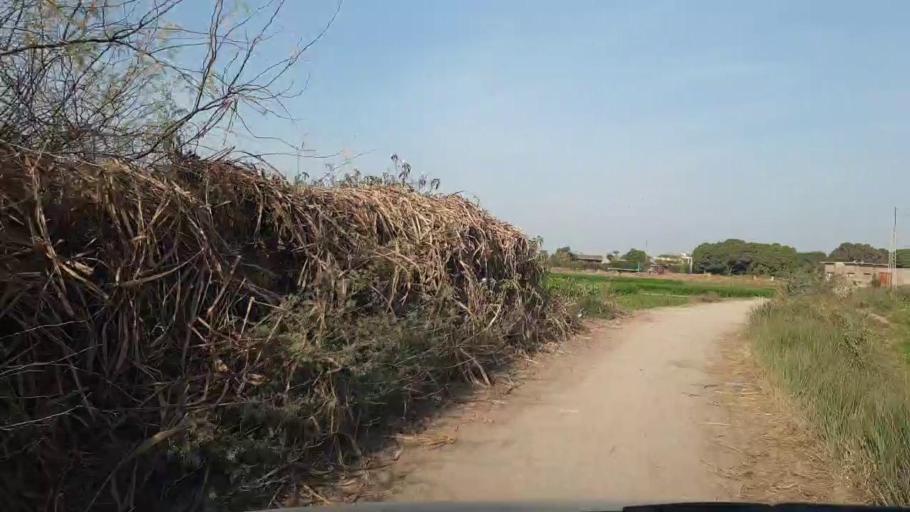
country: PK
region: Sindh
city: Chambar
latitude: 25.3267
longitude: 68.7544
